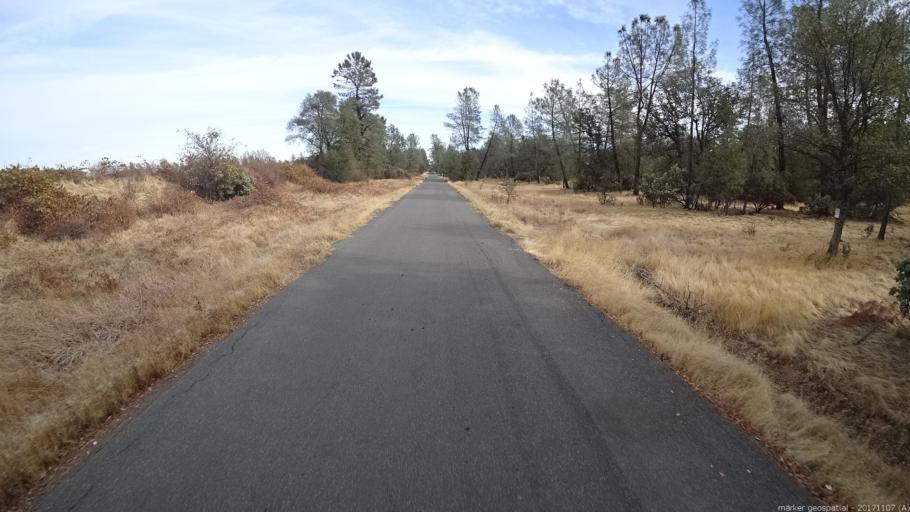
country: US
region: California
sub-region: Shasta County
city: Shasta
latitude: 40.4772
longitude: -122.4894
